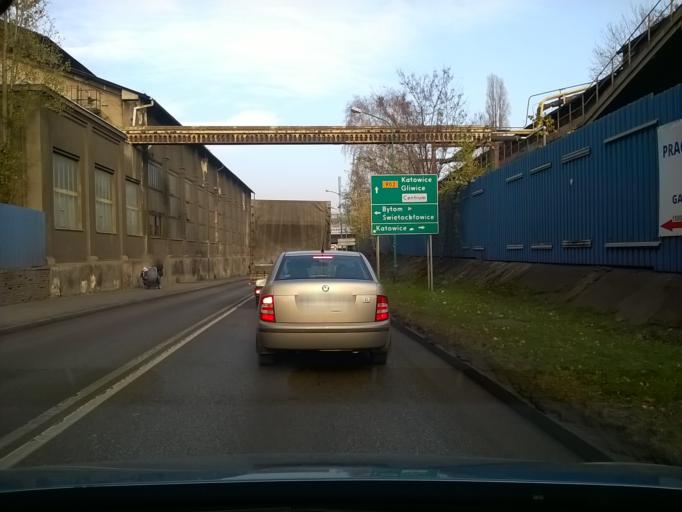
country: PL
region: Silesian Voivodeship
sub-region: Swietochlowice
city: Swietochlowice
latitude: 50.2777
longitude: 18.9424
